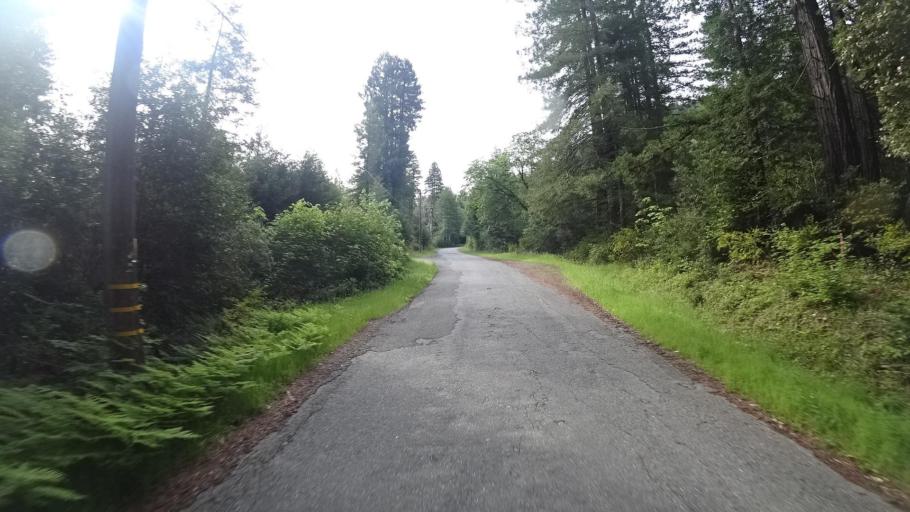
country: US
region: California
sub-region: Humboldt County
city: Redway
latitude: 40.3419
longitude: -123.9159
